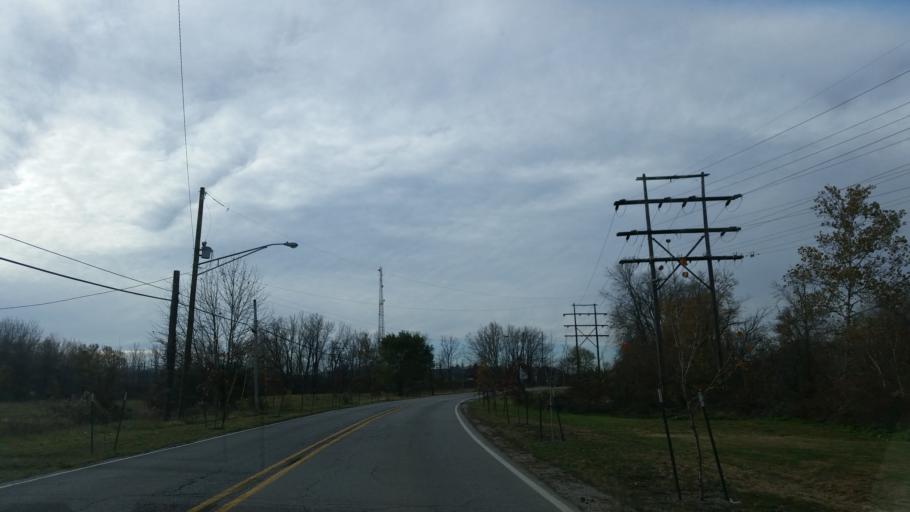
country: US
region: Indiana
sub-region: Howard County
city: Kokomo
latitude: 40.4729
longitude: -86.1495
